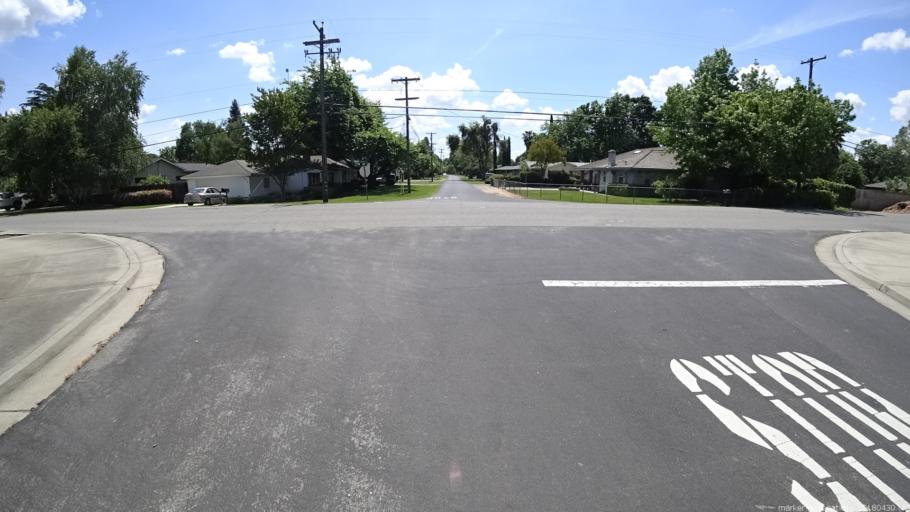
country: US
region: California
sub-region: Yolo County
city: West Sacramento
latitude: 38.5440
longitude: -121.5237
